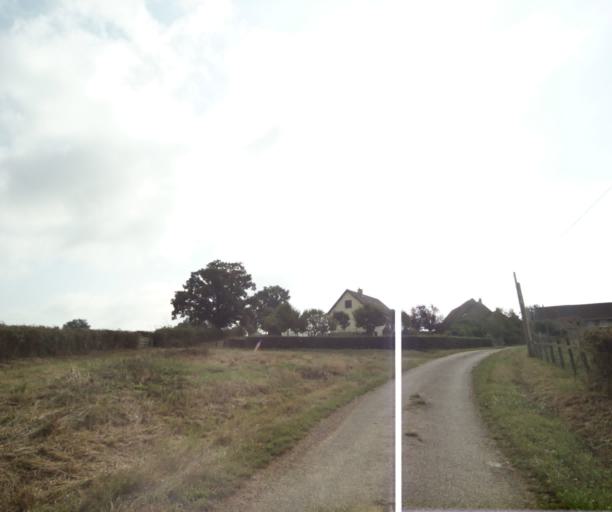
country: FR
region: Bourgogne
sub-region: Departement de Saone-et-Loire
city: Charolles
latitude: 46.4280
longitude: 4.2828
